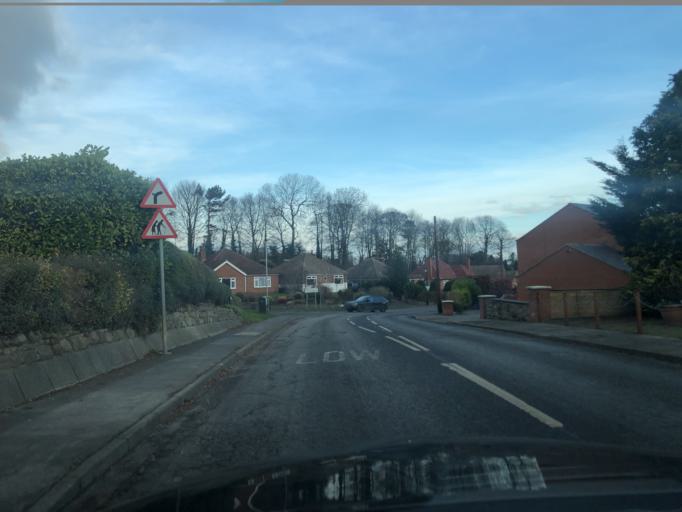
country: GB
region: England
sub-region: North Yorkshire
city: Bedale
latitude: 54.2860
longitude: -1.5975
